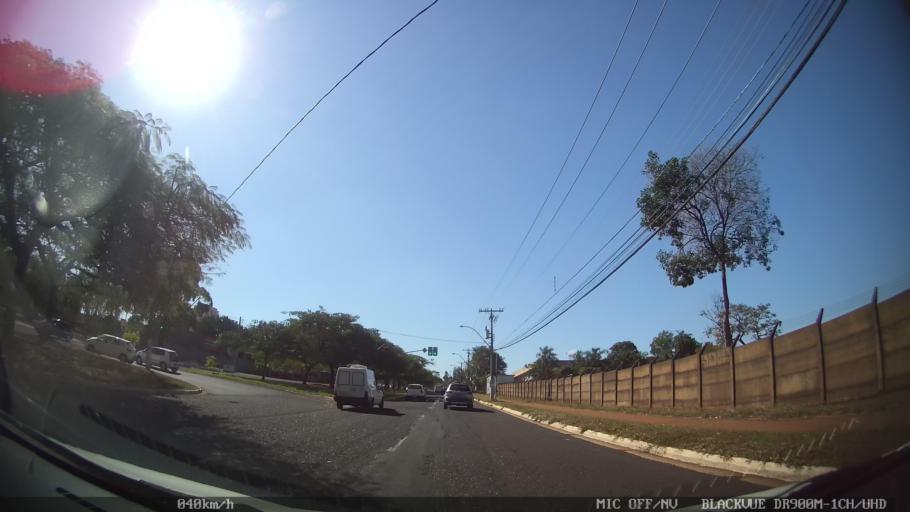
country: BR
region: Sao Paulo
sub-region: Ribeirao Preto
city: Ribeirao Preto
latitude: -21.2048
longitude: -47.7688
